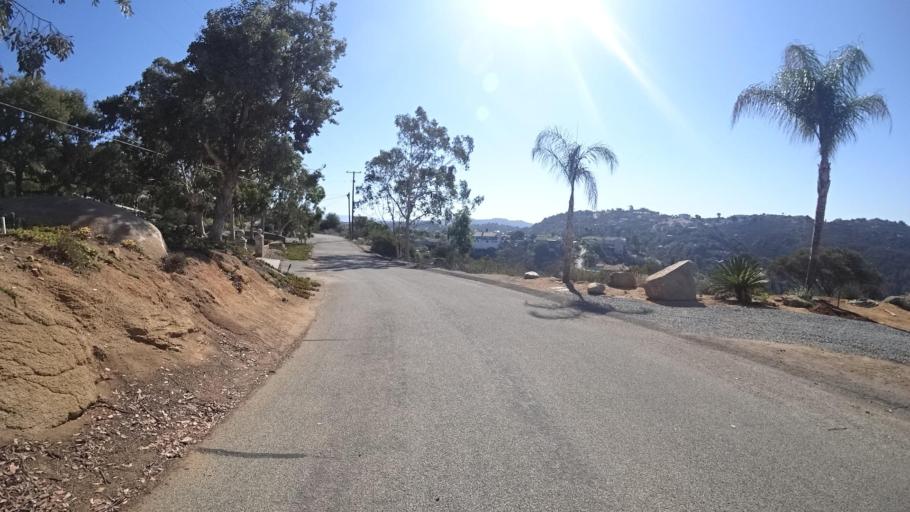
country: US
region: California
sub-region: San Diego County
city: Hidden Meadows
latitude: 33.2173
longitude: -117.1255
